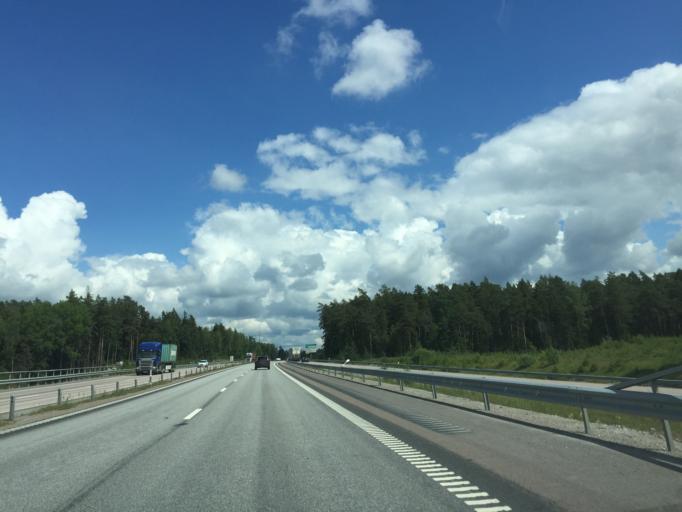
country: SE
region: Vaestmanland
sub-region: Vasteras
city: Vasteras
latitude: 59.5998
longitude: 16.4372
